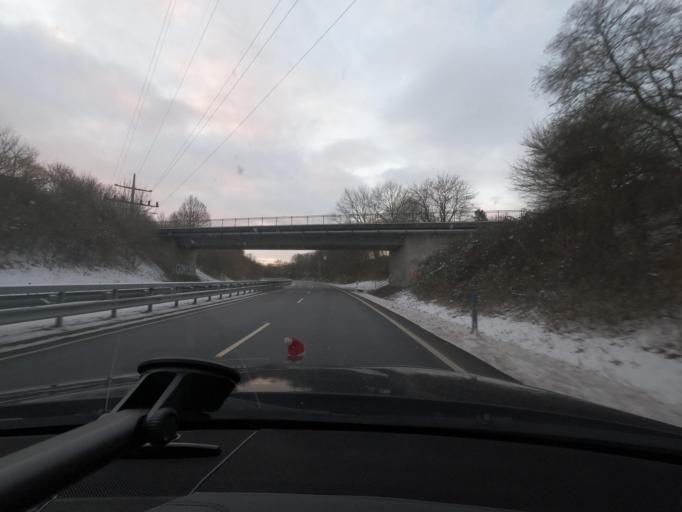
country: DE
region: Schleswig-Holstein
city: Harrislee
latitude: 54.8063
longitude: 9.4046
